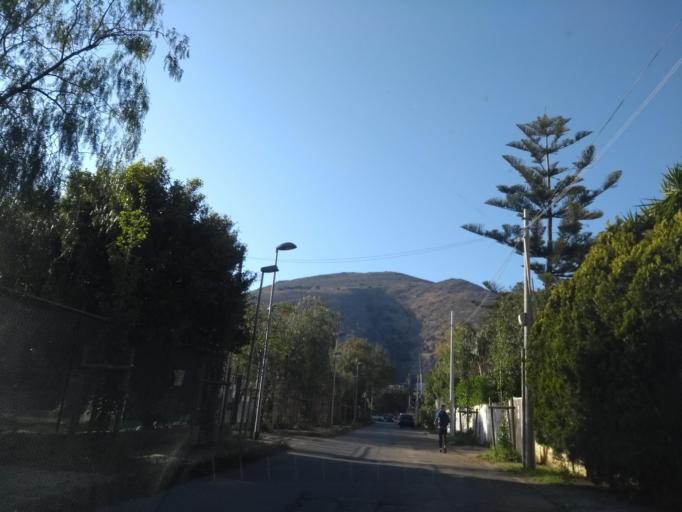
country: IT
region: Sicily
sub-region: Palermo
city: Palermo
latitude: 38.2003
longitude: 13.3245
